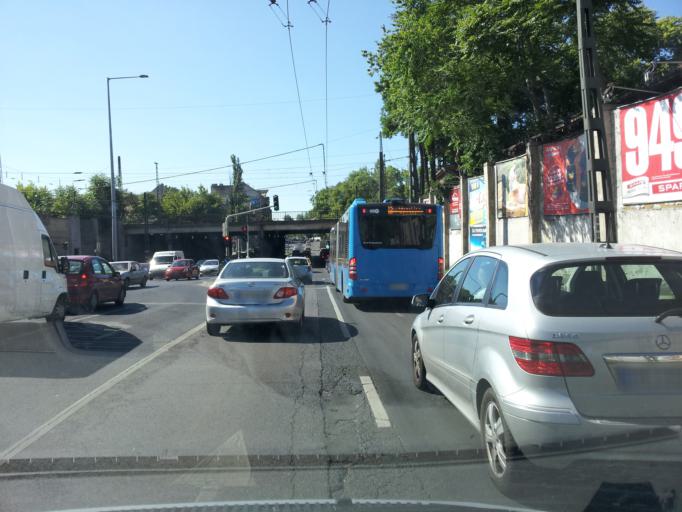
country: HU
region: Budapest
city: Budapest XIII. keruelet
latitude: 47.5175
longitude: 19.0738
